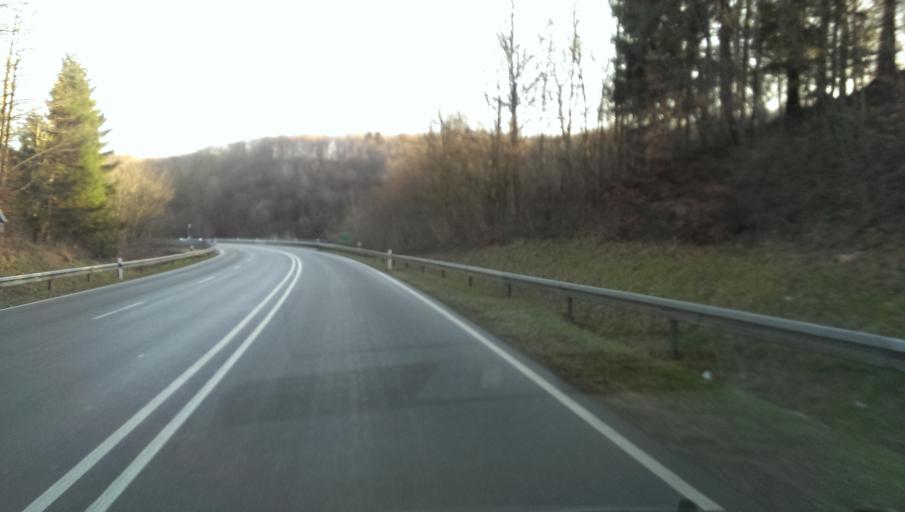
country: DE
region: North Rhine-Westphalia
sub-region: Regierungsbezirk Detmold
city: Bad Driburg
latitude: 51.7339
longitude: 8.9955
